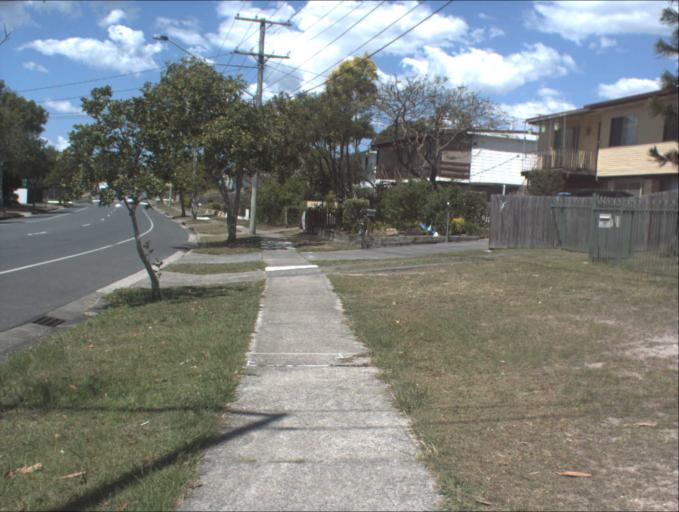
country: AU
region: Queensland
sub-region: Logan
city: Logan City
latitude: -27.6572
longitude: 153.0972
